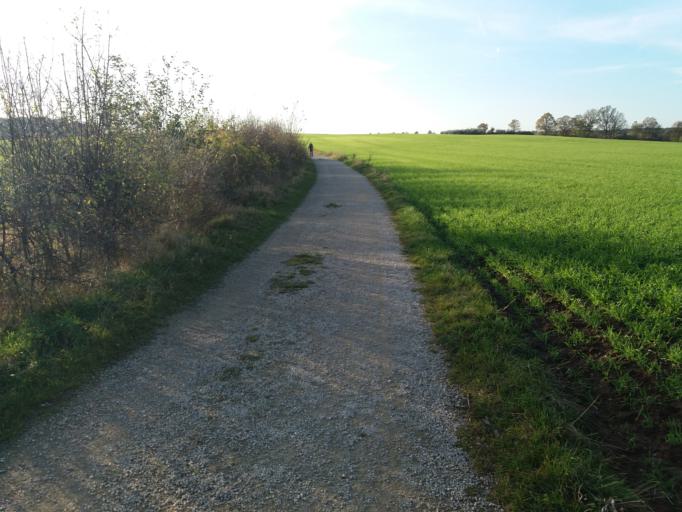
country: DE
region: Bavaria
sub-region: Regierungsbezirk Mittelfranken
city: Zirndorf
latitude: 49.4415
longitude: 10.9333
